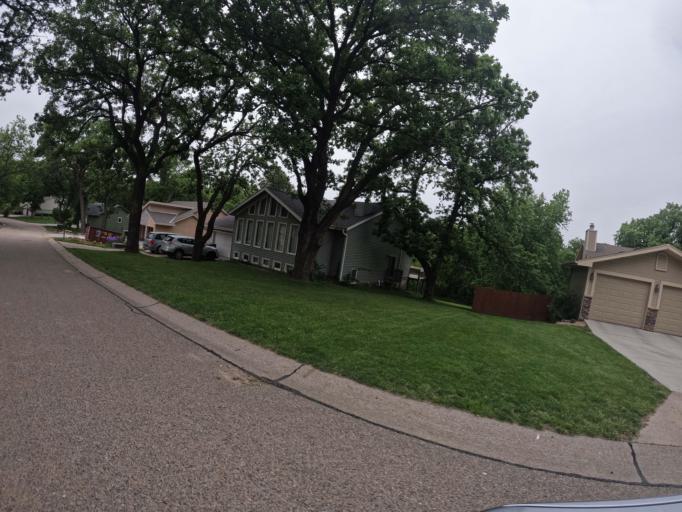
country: US
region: Nebraska
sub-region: Sarpy County
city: Offutt Air Force Base
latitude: 41.0508
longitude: -95.9694
